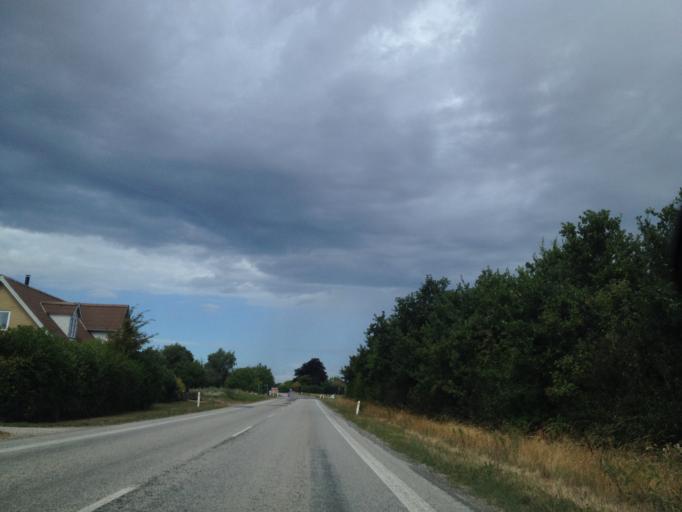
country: DK
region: Zealand
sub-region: Guldborgsund Kommune
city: Sakskobing
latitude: 54.7600
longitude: 11.6638
